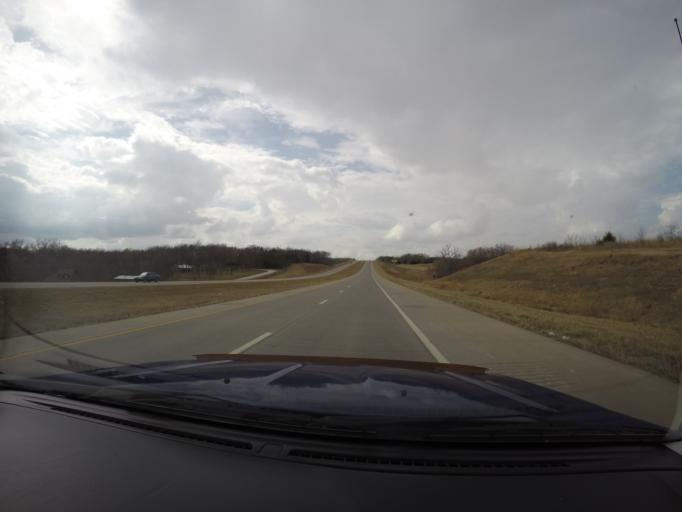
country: US
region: Kansas
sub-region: Pottawatomie County
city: Wamego
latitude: 39.2104
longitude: -96.3345
